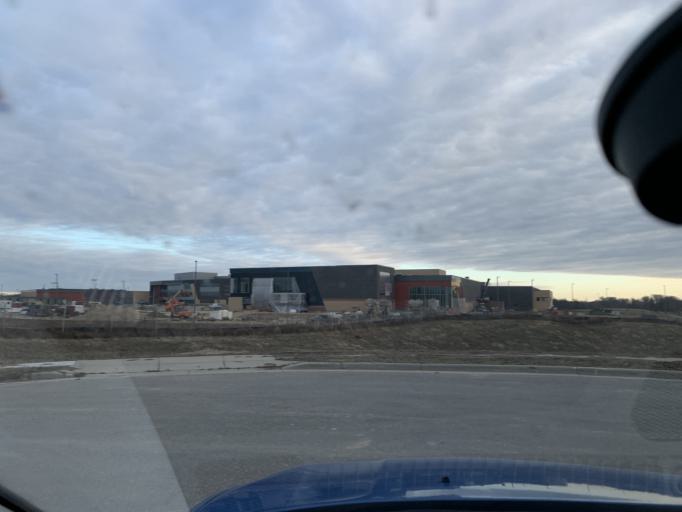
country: US
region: Wisconsin
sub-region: Dane County
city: Verona
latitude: 42.9862
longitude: -89.5569
